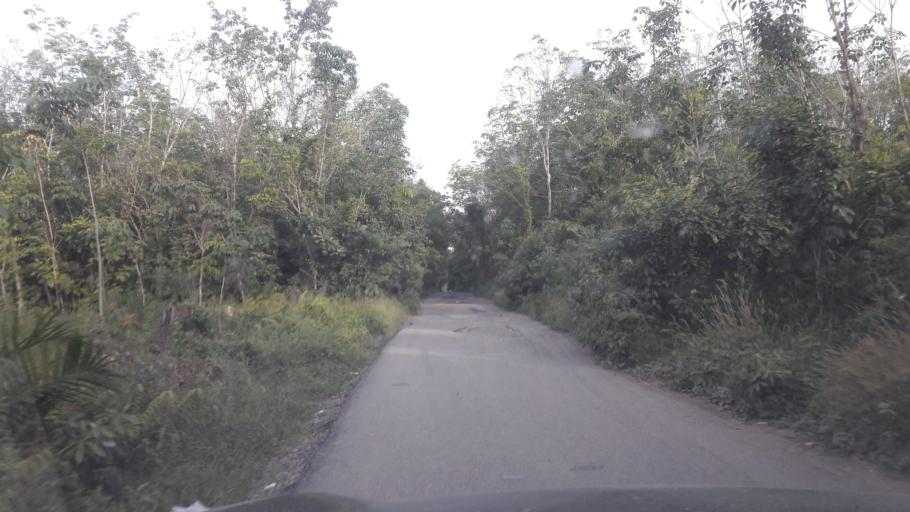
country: ID
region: South Sumatra
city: Gunungmenang
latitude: -3.2745
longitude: 104.0781
